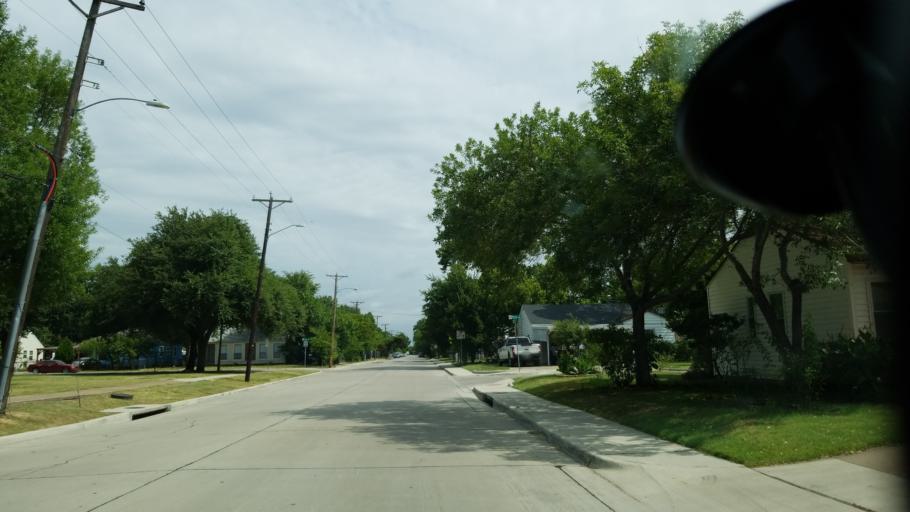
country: US
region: Texas
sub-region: Dallas County
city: Grand Prairie
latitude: 32.7518
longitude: -96.9860
